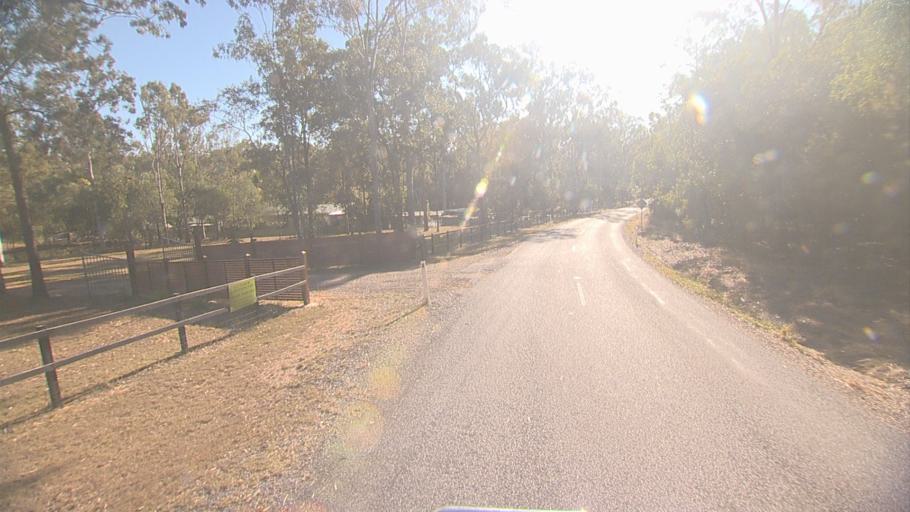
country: AU
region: Queensland
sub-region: Logan
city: North Maclean
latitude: -27.7856
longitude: 152.9623
